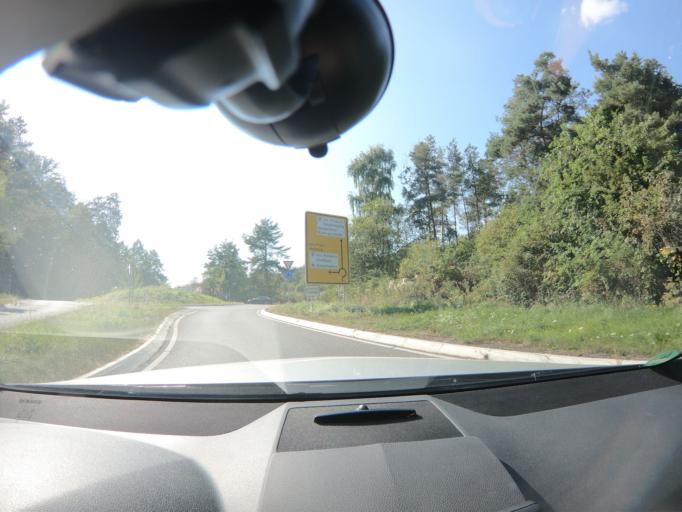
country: DE
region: Hesse
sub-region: Regierungsbezirk Giessen
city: Colbe
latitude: 50.8175
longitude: 8.8094
